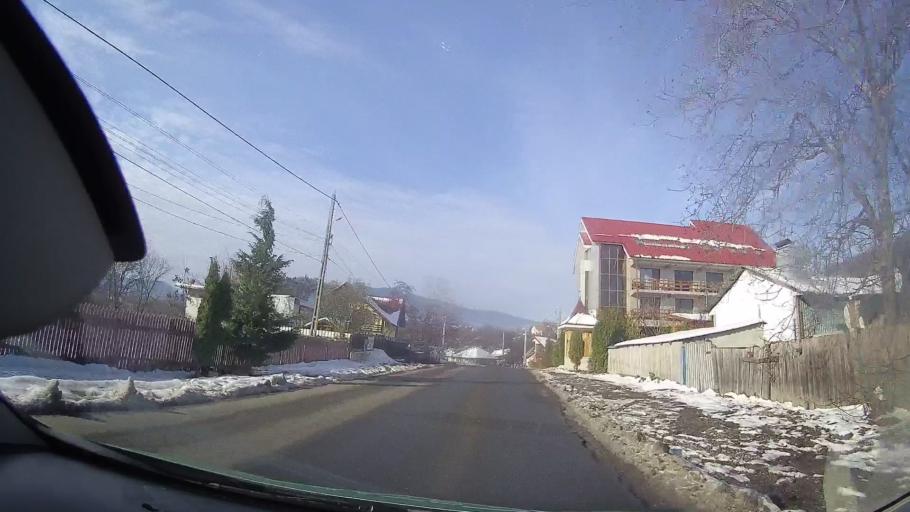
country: RO
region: Neamt
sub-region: Comuna Garcina
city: Garcina
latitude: 46.9736
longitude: 26.3622
